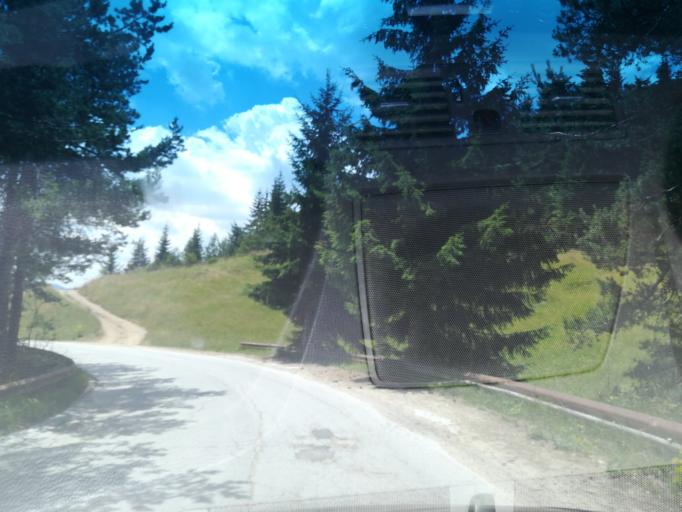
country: BG
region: Smolyan
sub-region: Obshtina Chepelare
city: Chepelare
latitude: 41.6936
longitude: 24.7685
